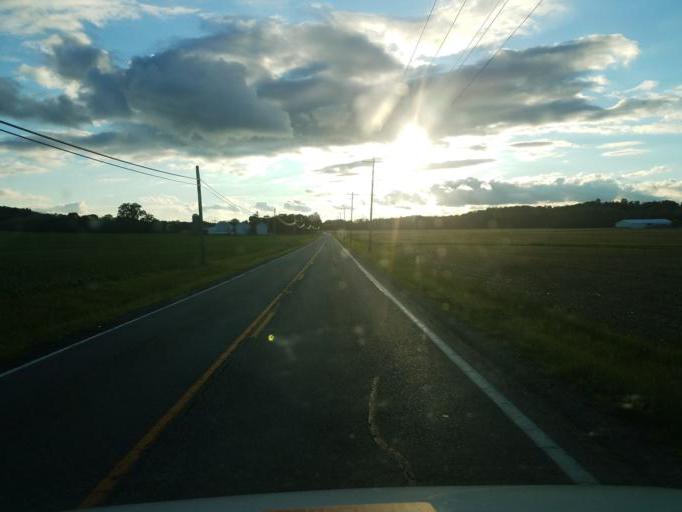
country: US
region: Ohio
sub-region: Knox County
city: Mount Vernon
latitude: 40.3976
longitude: -82.5268
